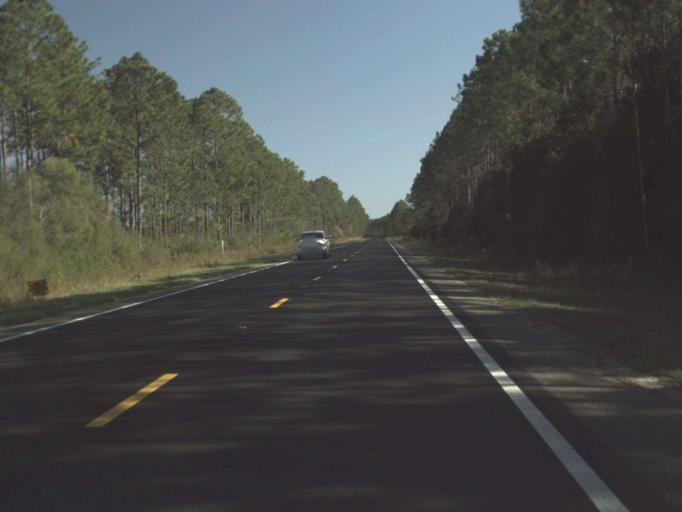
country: US
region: Florida
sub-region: Gulf County
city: Port Saint Joe
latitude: 29.7459
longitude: -85.2362
